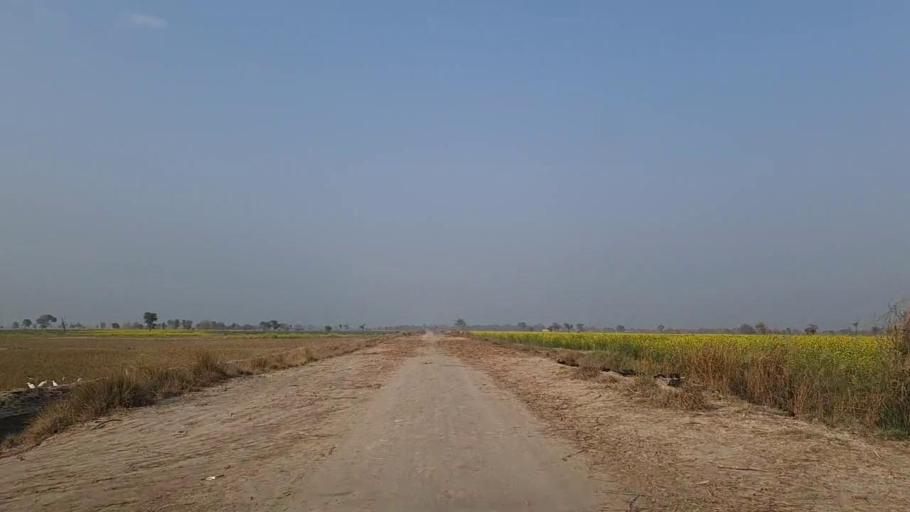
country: PK
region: Sindh
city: Jam Sahib
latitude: 26.3355
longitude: 68.5148
